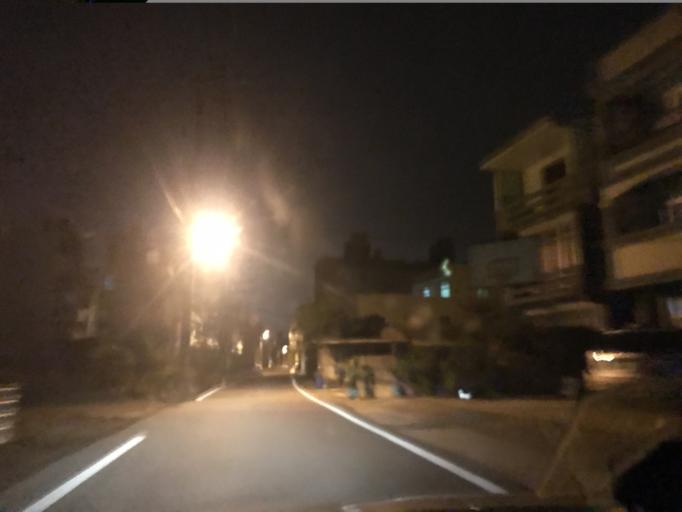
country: TW
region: Taiwan
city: Daxi
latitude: 24.8472
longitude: 121.2242
